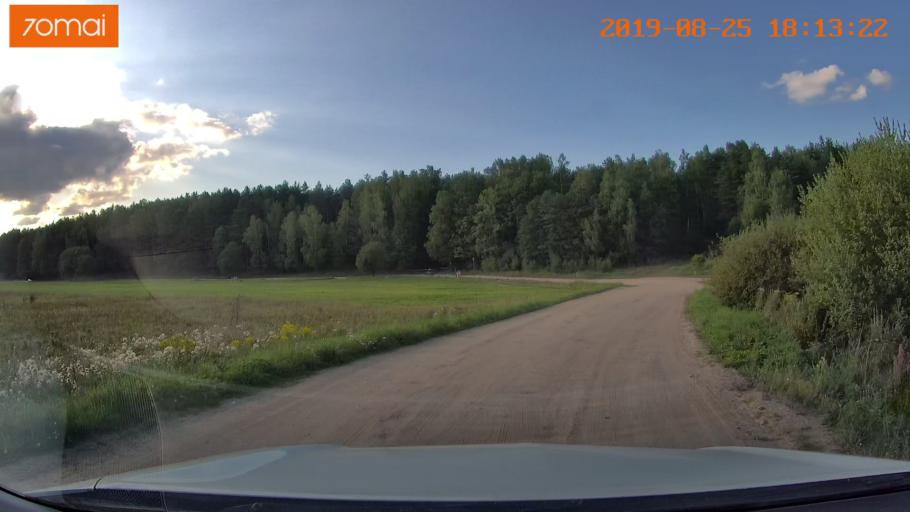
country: BY
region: Minsk
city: Khatsyezhyna
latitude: 53.9436
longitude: 27.3068
